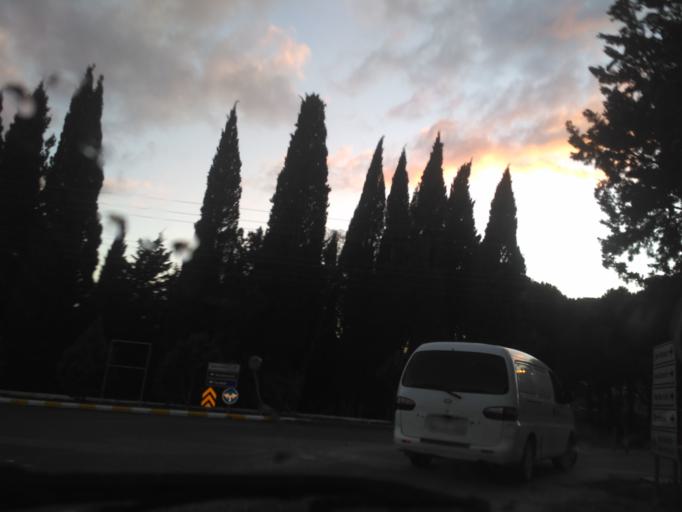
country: TR
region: Balikesir
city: Ayvalik
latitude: 39.3103
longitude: 26.7006
